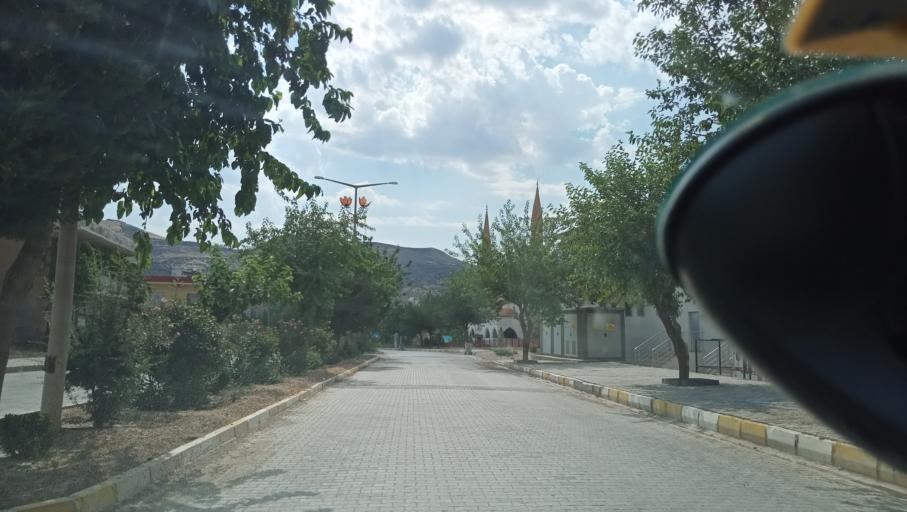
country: TR
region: Mardin
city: Yesilli
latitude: 37.3397
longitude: 40.8154
